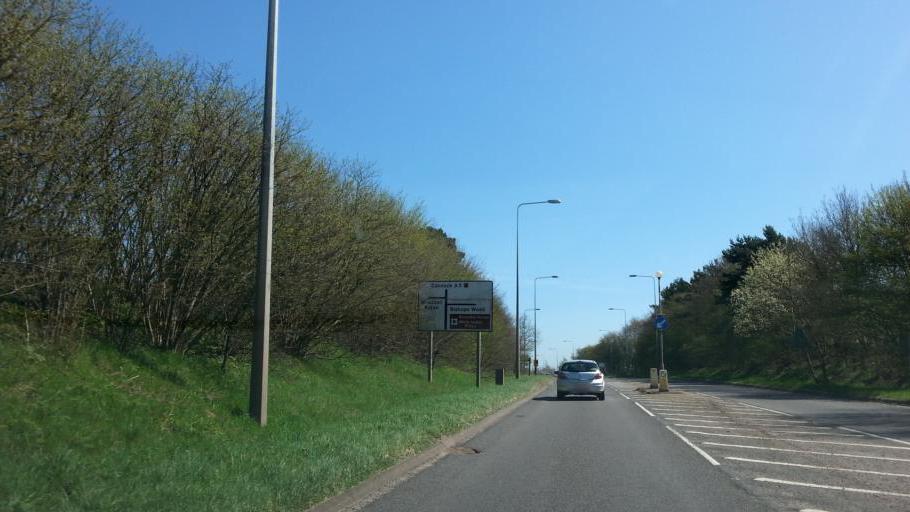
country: GB
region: England
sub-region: Staffordshire
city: Wheaton Aston
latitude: 52.6940
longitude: -2.2493
